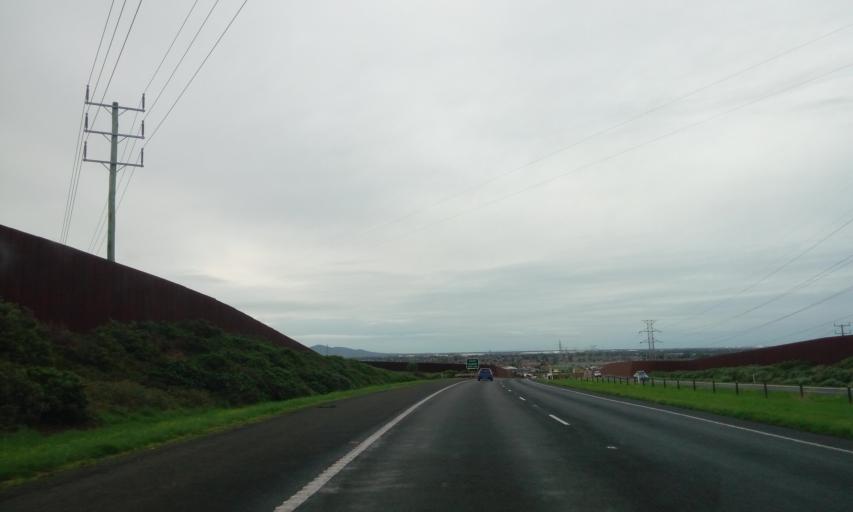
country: AU
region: Victoria
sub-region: Greater Geelong
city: Bell Post Hill
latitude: -38.0907
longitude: 144.3246
